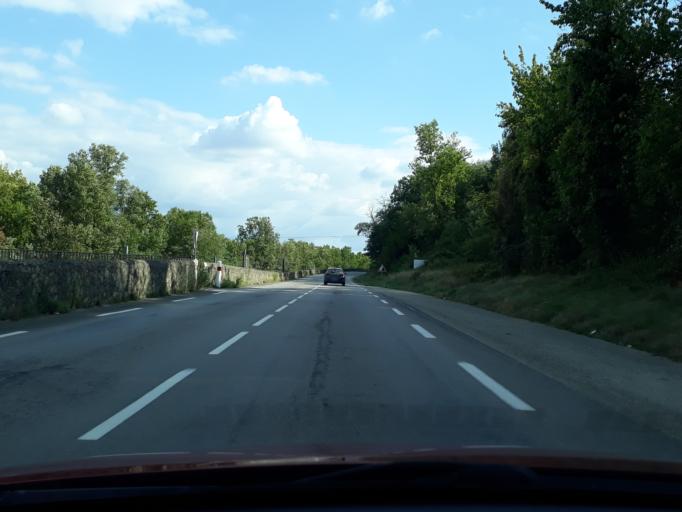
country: FR
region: Rhone-Alpes
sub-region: Departement de la Loire
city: Saint-Pierre-de-Boeuf
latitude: 45.3719
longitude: 4.7508
